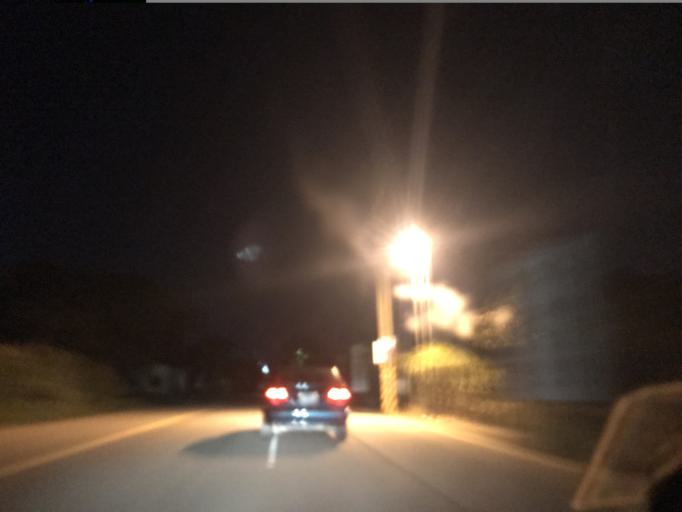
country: TW
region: Taiwan
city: Daxi
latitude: 24.8300
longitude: 121.1923
